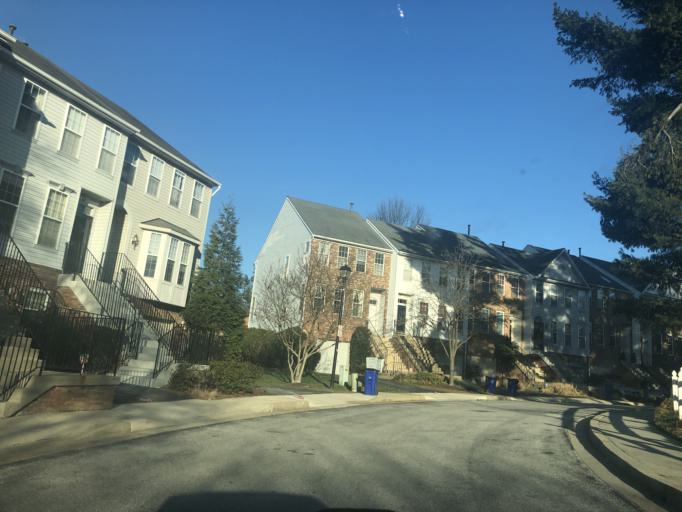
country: US
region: Maryland
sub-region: Howard County
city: Columbia
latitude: 39.2083
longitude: -76.8278
